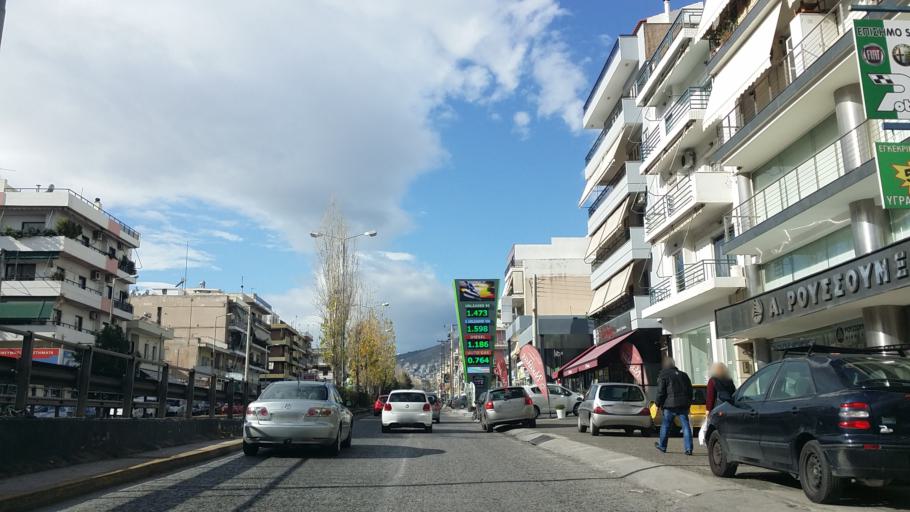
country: GR
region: Attica
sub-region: Nomos Piraios
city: Agios Ioannis Rentis
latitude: 37.9770
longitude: 23.6652
